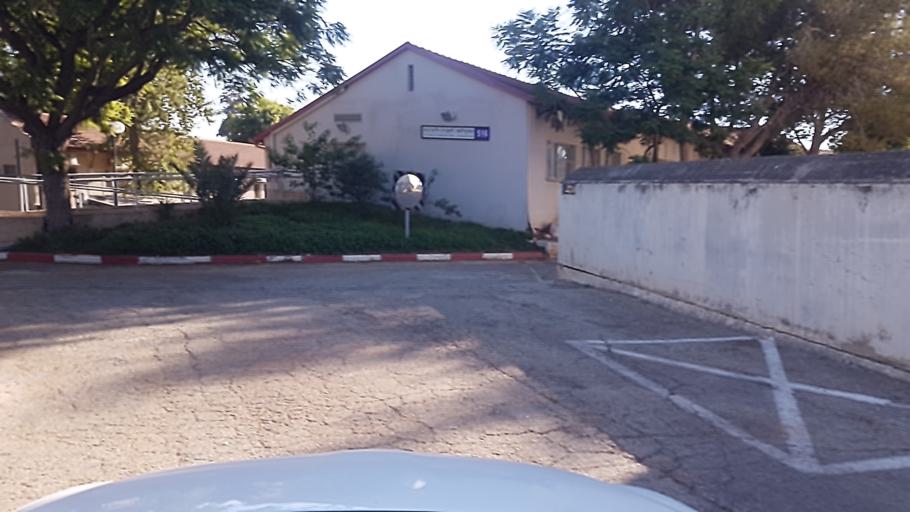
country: IL
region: Central District
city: Kfar Saba
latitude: 32.2004
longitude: 34.9266
